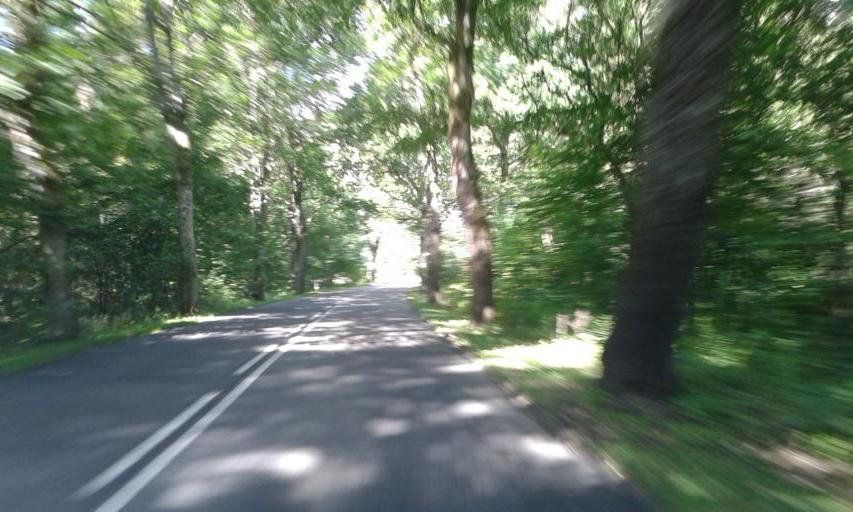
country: PL
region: West Pomeranian Voivodeship
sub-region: Powiat slawienski
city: Slawno
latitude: 54.2479
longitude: 16.6927
